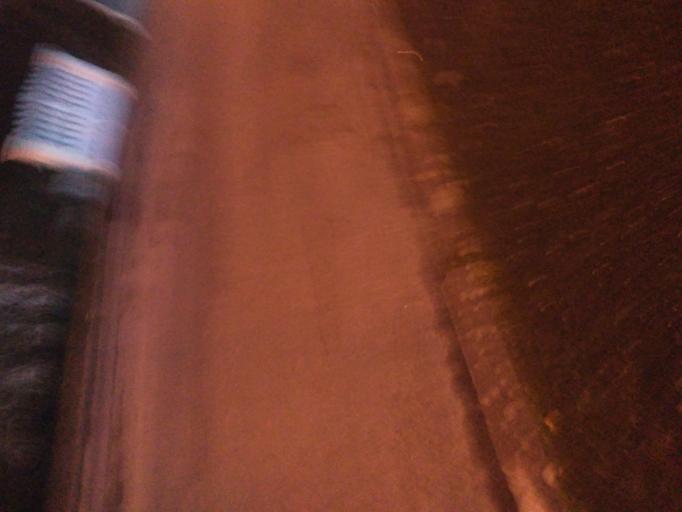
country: FR
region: Pays de la Loire
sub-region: Departement de la Loire-Atlantique
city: Saint-Sebastien-sur-Loire
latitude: 47.1916
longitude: -1.5057
